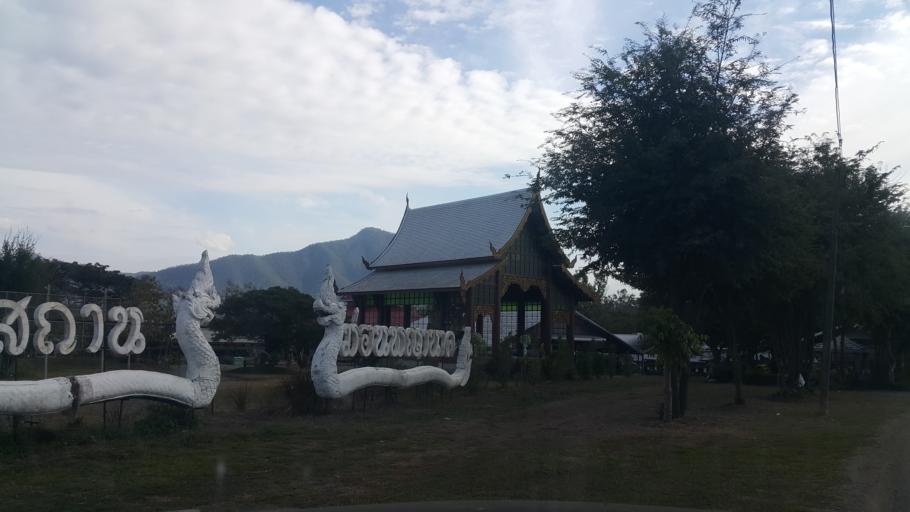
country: TH
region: Chiang Mai
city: Mae On
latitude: 18.7574
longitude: 99.2358
